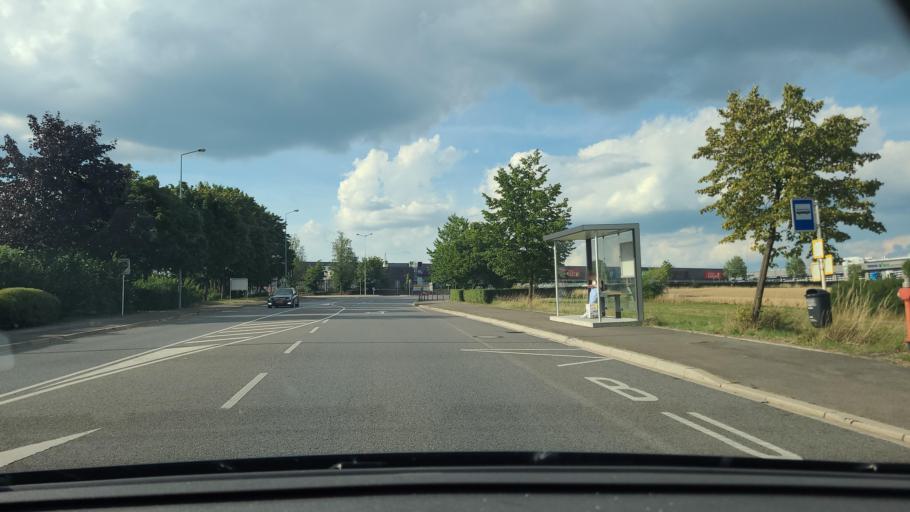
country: LU
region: Luxembourg
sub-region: Canton d'Esch-sur-Alzette
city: Bettembourg
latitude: 49.5288
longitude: 6.1018
